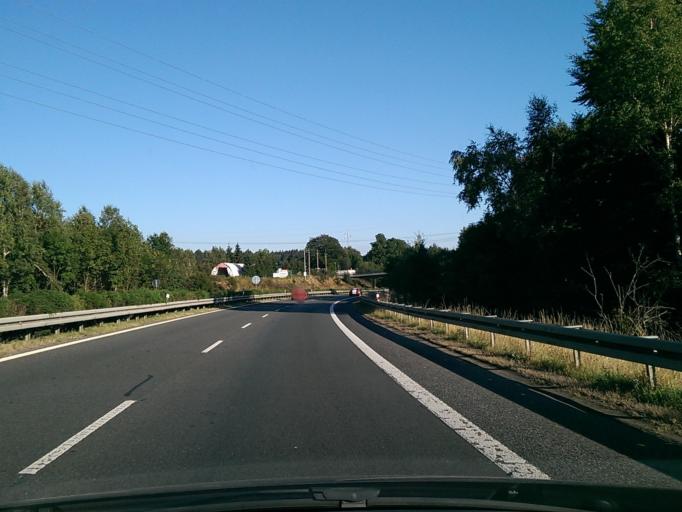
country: CZ
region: Liberecky
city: Hodkovice nad Mohelkou
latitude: 50.7089
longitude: 15.0881
